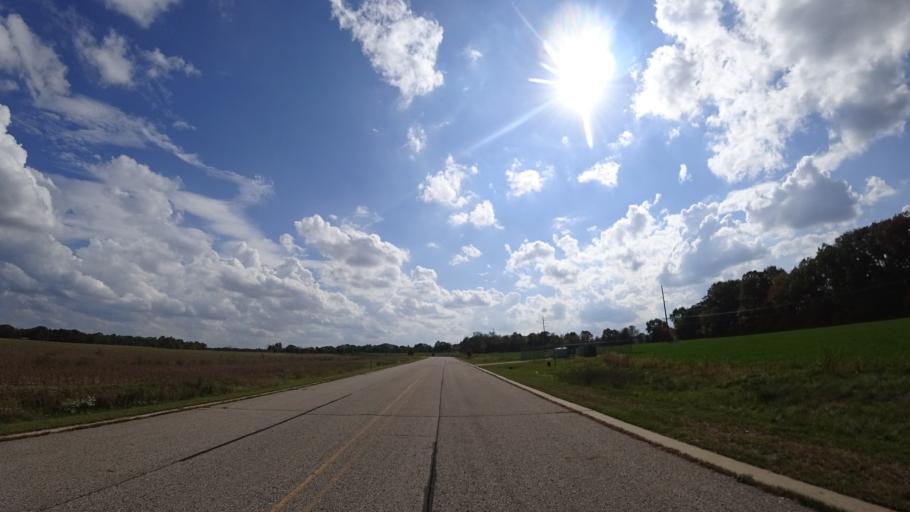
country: US
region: Michigan
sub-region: Saint Joseph County
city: Three Rivers
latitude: 41.9617
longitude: -85.6136
